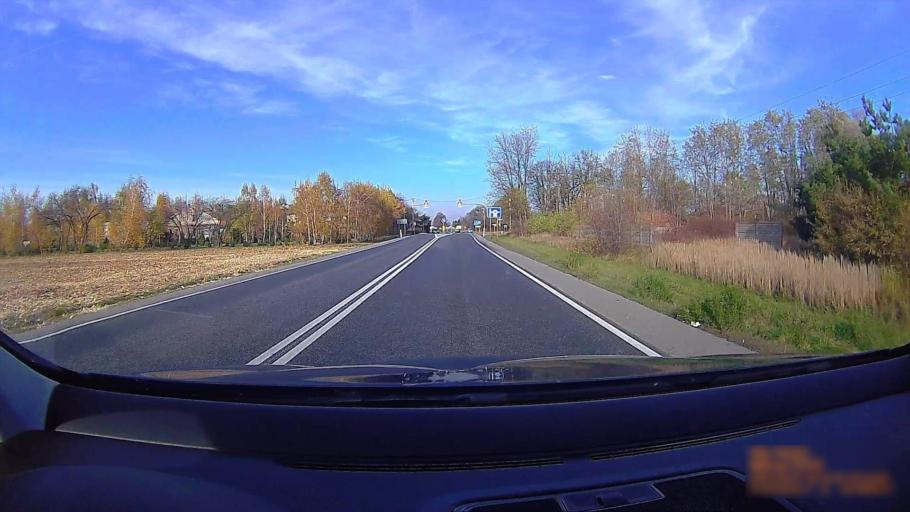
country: PL
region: Greater Poland Voivodeship
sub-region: Powiat koninski
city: Rychwal
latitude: 52.0768
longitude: 18.1597
